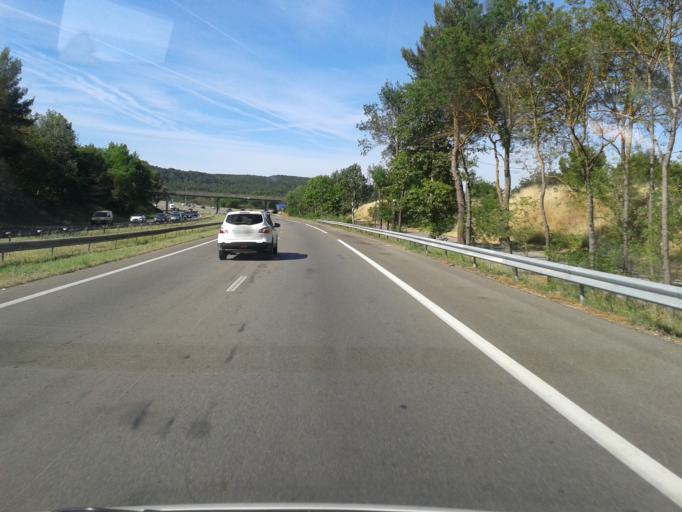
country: FR
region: Provence-Alpes-Cote d'Azur
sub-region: Departement des Bouches-du-Rhone
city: Bouc-Bel-Air
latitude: 43.4557
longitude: 5.3989
